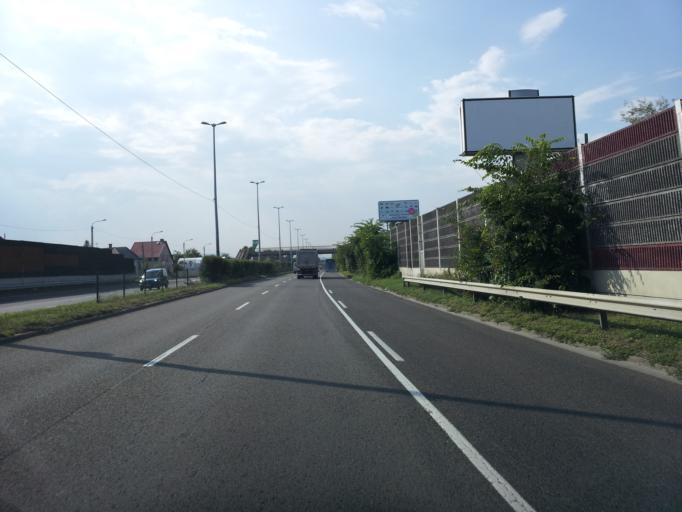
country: HU
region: Budapest
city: Budapest XIX. keruelet
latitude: 47.4400
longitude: 19.1368
